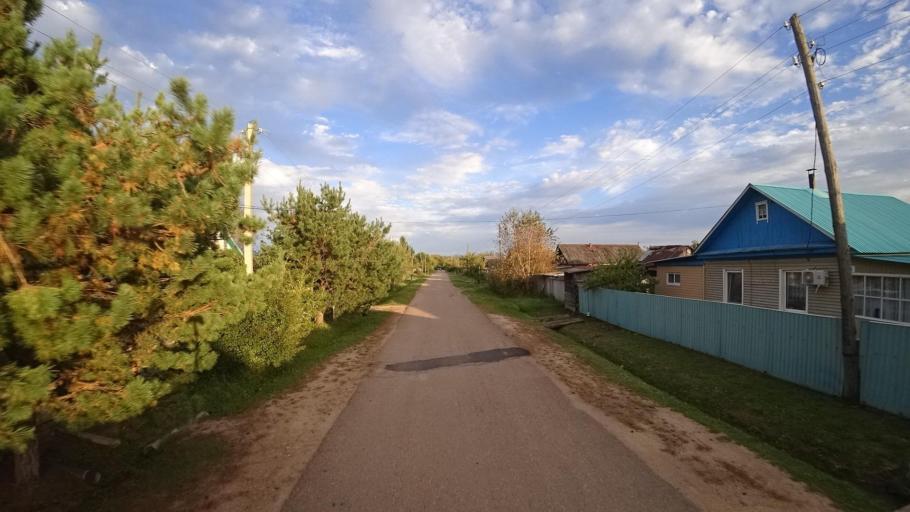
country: RU
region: Primorskiy
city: Yakovlevka
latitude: 44.4241
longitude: 133.4868
